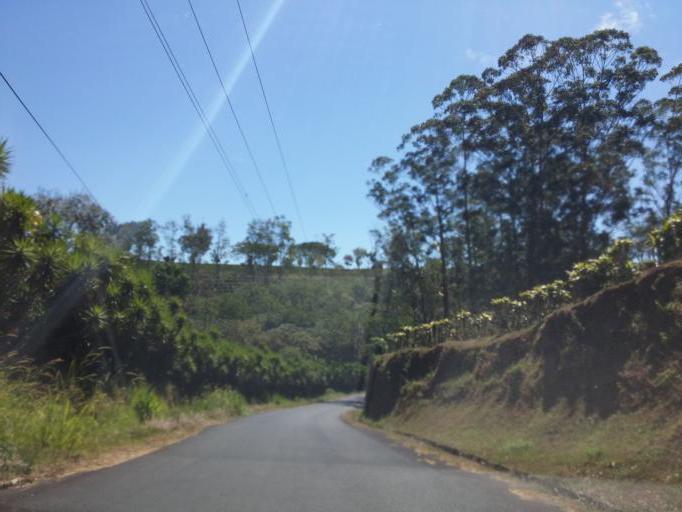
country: CR
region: Alajuela
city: Sabanilla
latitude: 10.0656
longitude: -84.2076
